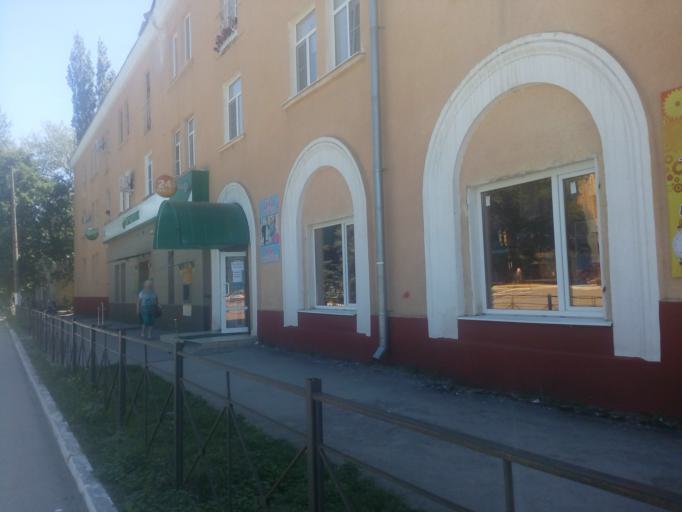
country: RU
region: Rostov
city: Sholokhovskiy
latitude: 48.2823
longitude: 41.0467
